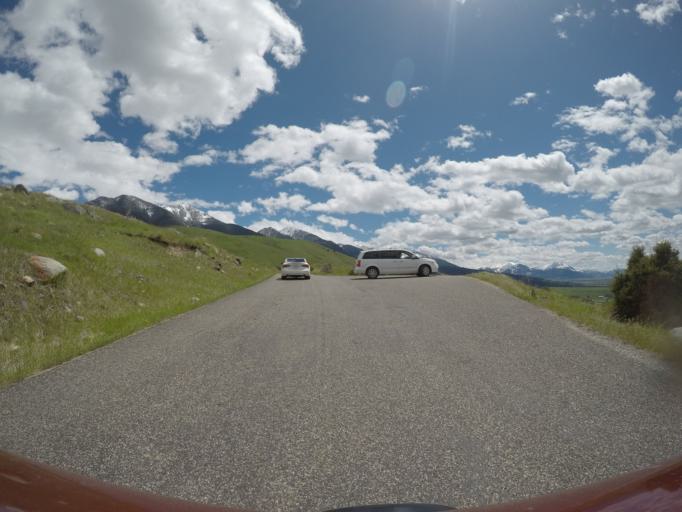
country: US
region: Montana
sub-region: Park County
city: Livingston
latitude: 45.4995
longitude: -110.5563
